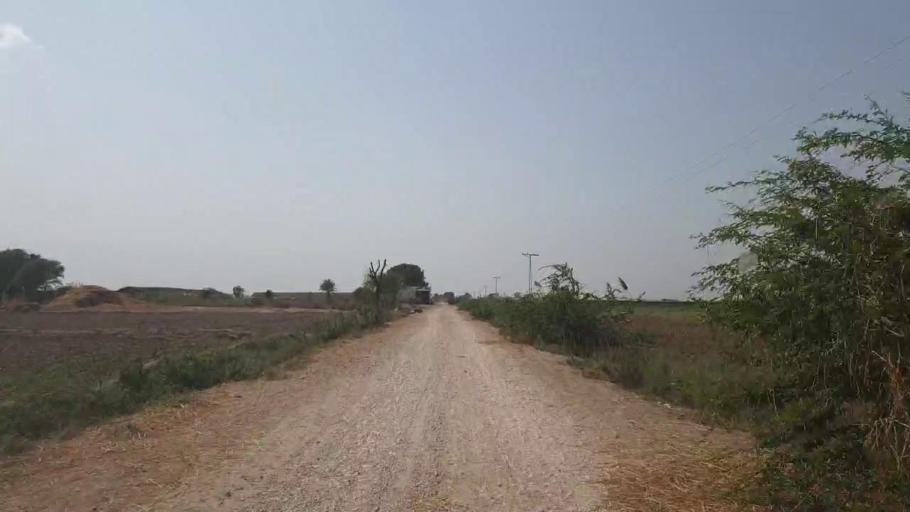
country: PK
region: Sindh
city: Jati
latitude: 24.4920
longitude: 68.5338
